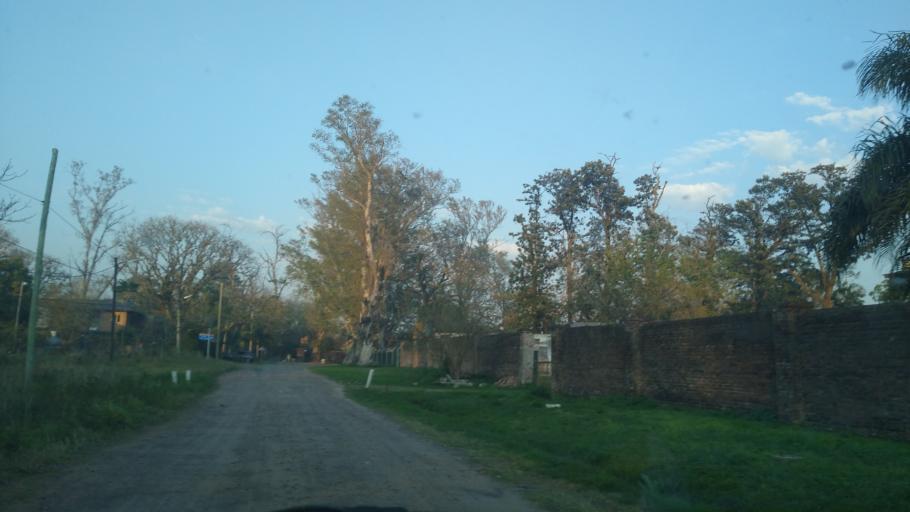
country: AR
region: Chaco
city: Barranqueras
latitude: -27.4664
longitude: -58.9566
